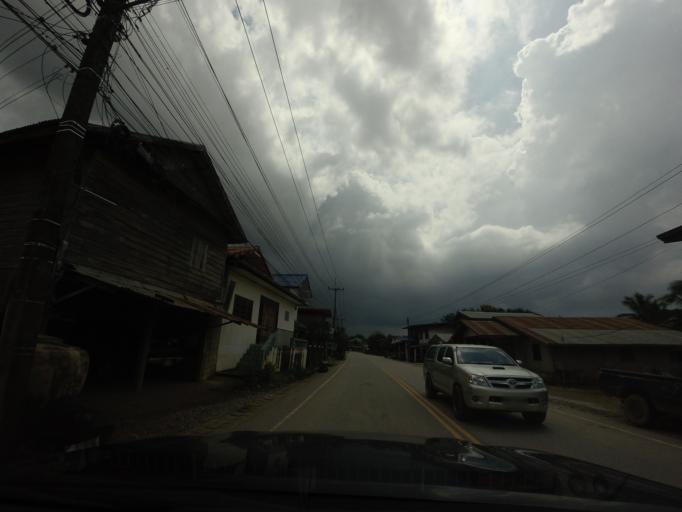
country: LA
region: Vientiane
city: Muang Sanakham
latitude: 17.9887
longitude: 101.7470
